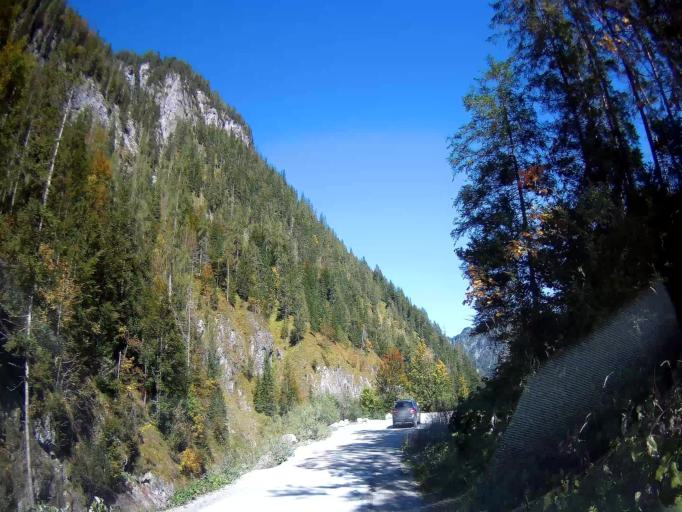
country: AT
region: Salzburg
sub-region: Politischer Bezirk Zell am See
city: Sankt Martin bei Lofer
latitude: 47.5217
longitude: 12.7070
